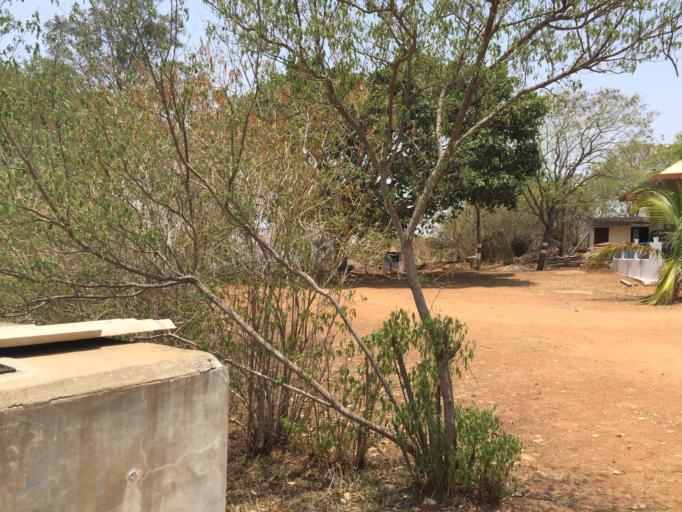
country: IN
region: Karnataka
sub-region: Bangalore Urban
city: Bangalore
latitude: 12.8880
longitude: 77.5283
